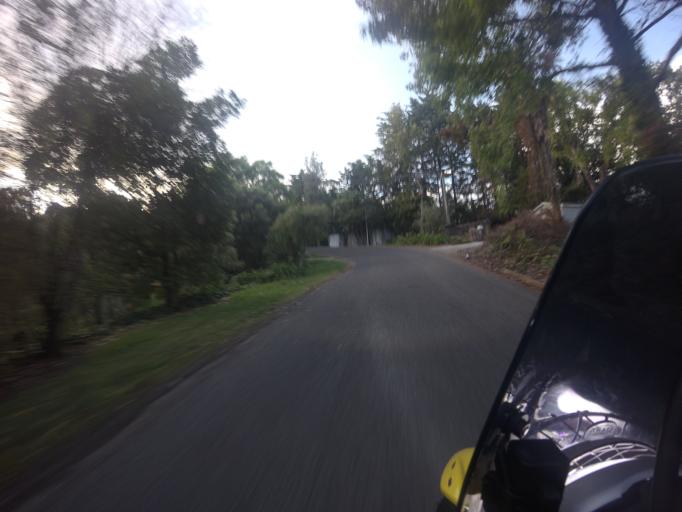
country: NZ
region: Gisborne
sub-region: Gisborne District
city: Gisborne
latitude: -38.6660
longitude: 178.0532
